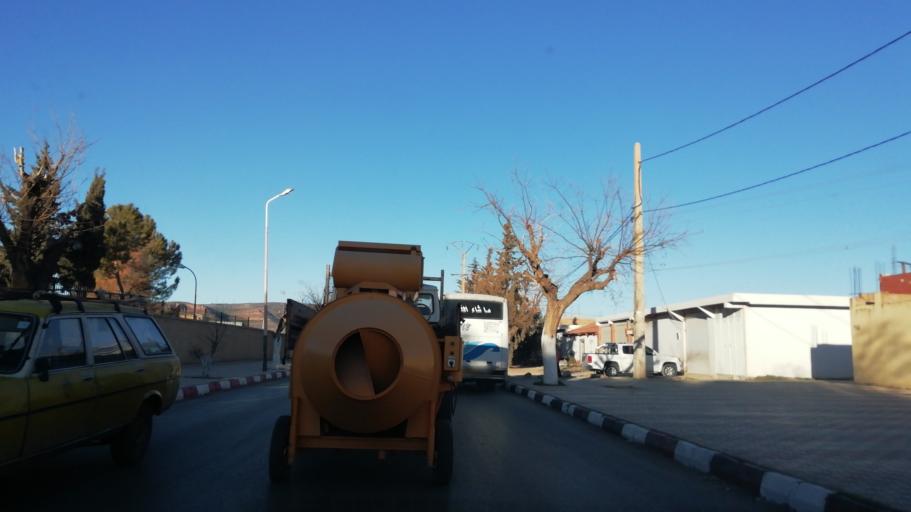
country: DZ
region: Tlemcen
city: Sebdou
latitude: 34.6497
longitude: -1.3201
